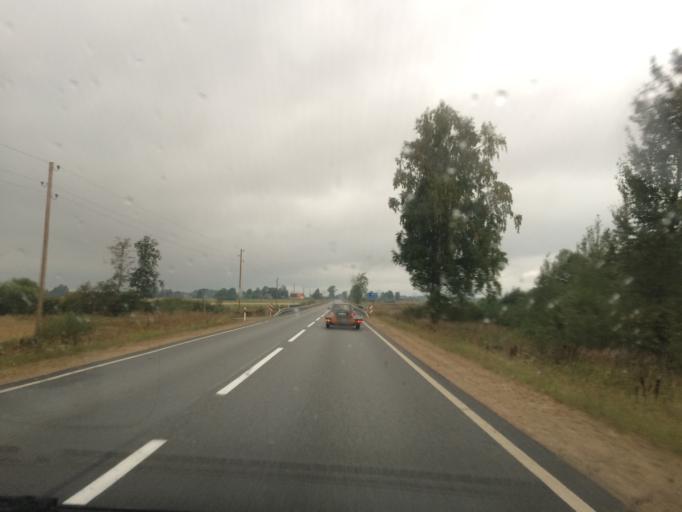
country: LV
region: Livani
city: Livani
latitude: 56.5326
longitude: 26.3348
